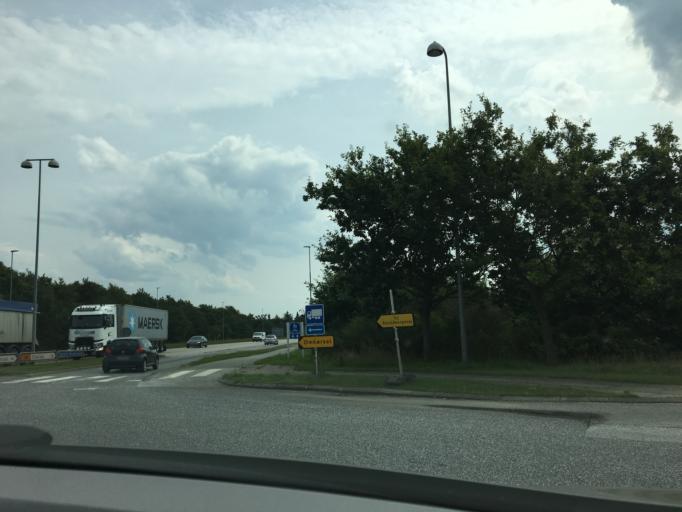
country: DK
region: Central Jutland
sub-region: Skive Kommune
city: Skive
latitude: 56.5438
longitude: 9.0324
